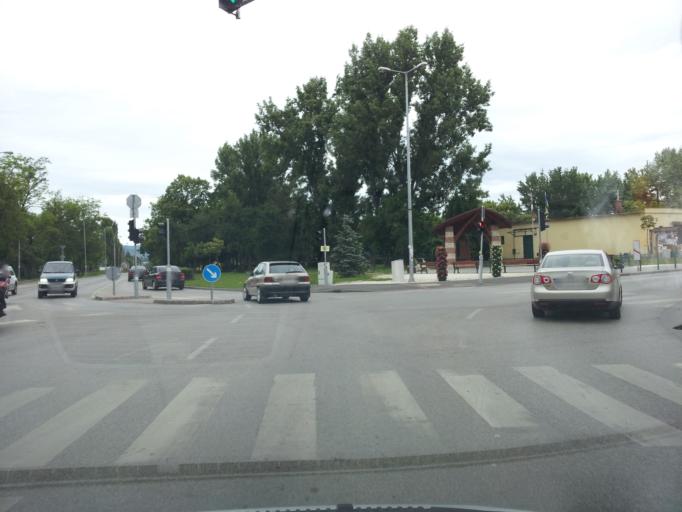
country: HU
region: Pest
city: Budakalasz
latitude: 47.6214
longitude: 19.0460
